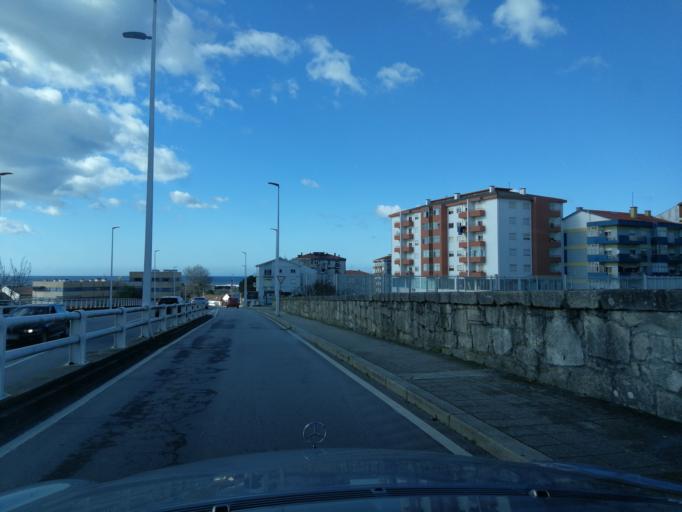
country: PT
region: Viana do Castelo
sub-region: Viana do Castelo
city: Viana do Castelo
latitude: 41.6946
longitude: -8.8382
